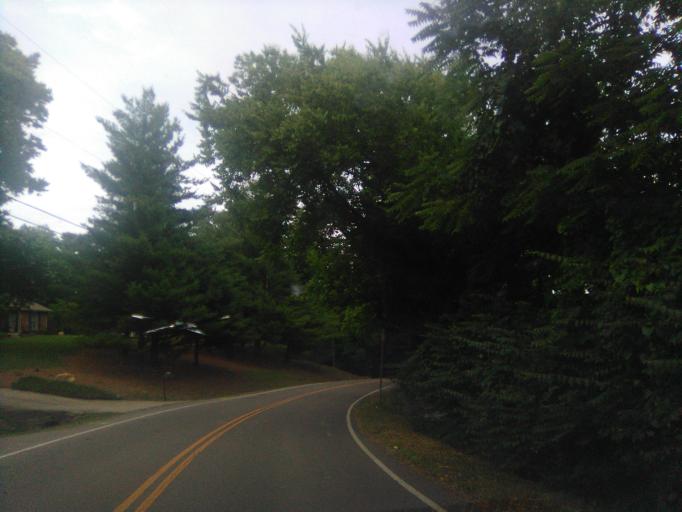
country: US
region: Tennessee
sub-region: Davidson County
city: Belle Meade
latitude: 36.0889
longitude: -86.8939
